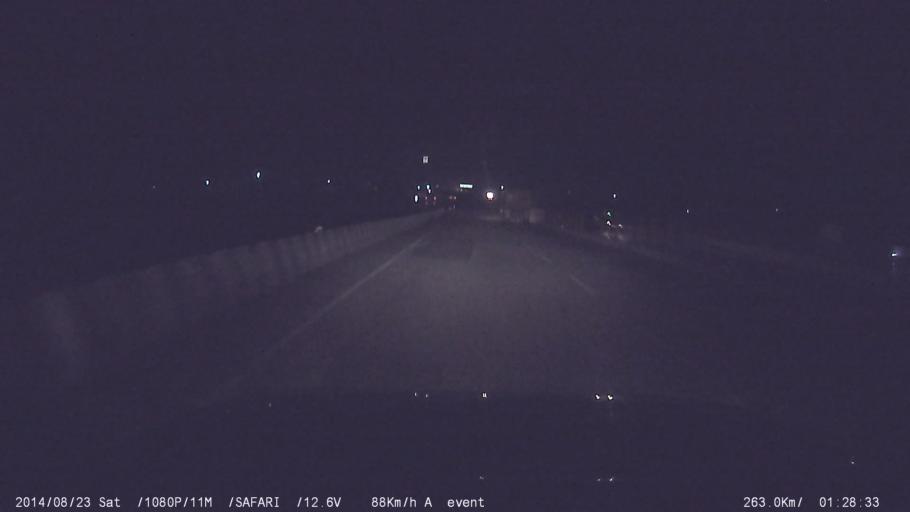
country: IN
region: Tamil Nadu
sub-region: Kancheepuram
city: Kanchipuram
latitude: 12.8741
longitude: 79.6938
